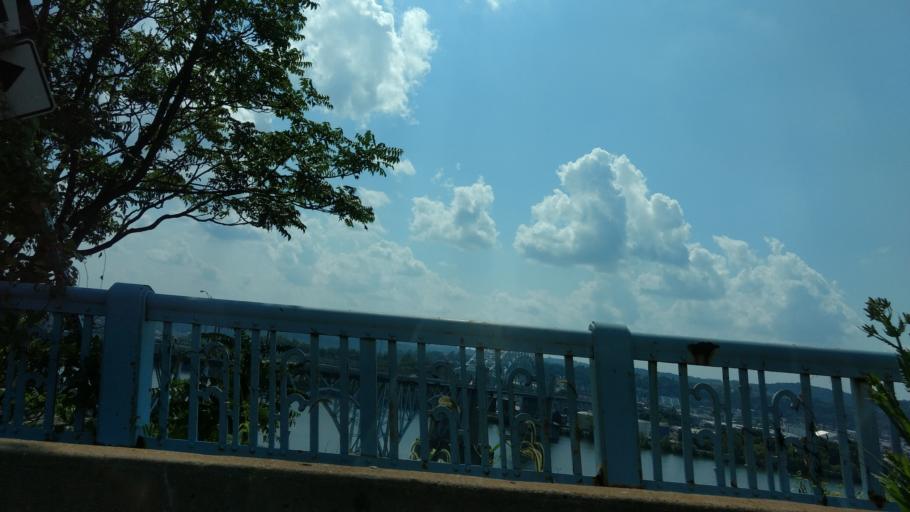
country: US
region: Pennsylvania
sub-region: Allegheny County
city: Bellevue
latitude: 40.4794
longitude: -80.0438
